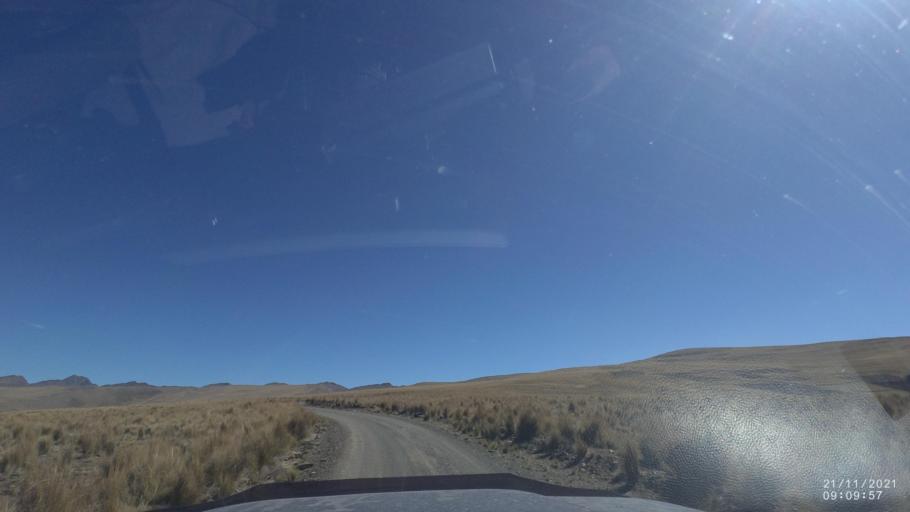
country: BO
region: Cochabamba
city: Cochabamba
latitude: -17.1567
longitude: -66.2594
